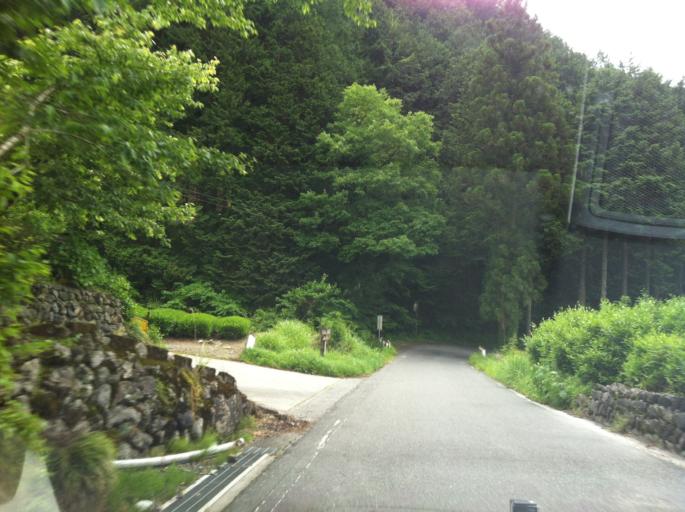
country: JP
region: Shizuoka
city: Shizuoka-shi
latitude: 35.1446
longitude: 138.3306
